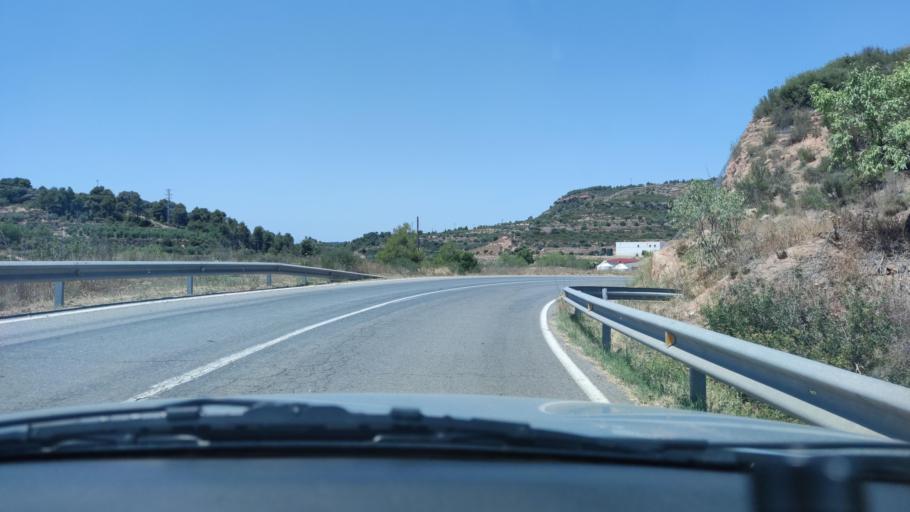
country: ES
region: Catalonia
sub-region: Provincia de Lleida
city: Juncosa
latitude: 41.3750
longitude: 0.7743
